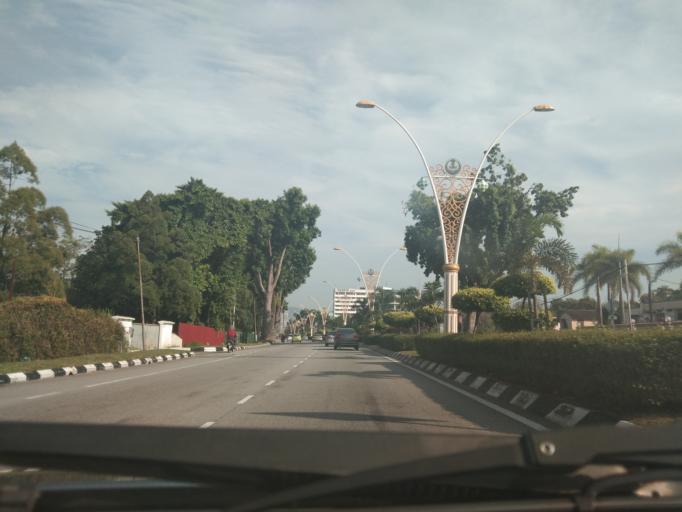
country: MY
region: Perak
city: Ipoh
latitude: 4.5873
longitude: 101.0978
